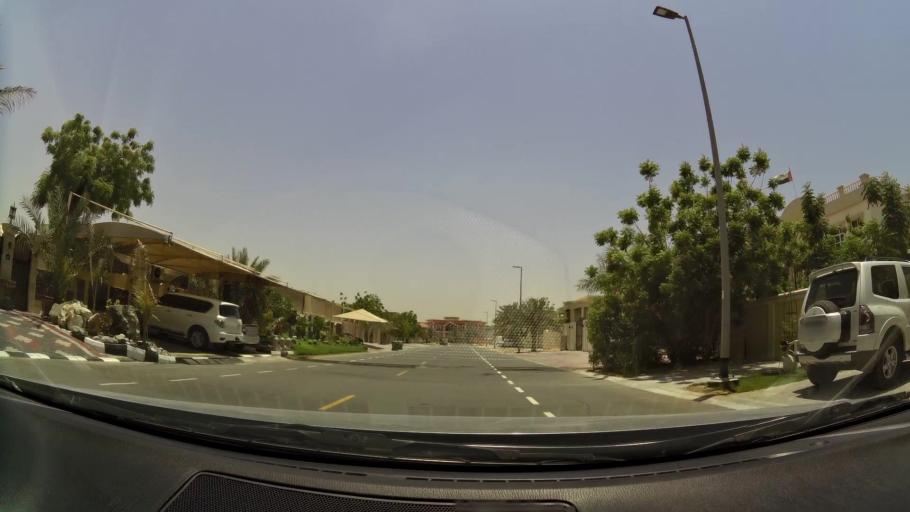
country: AE
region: Dubai
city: Dubai
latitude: 25.0963
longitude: 55.1869
